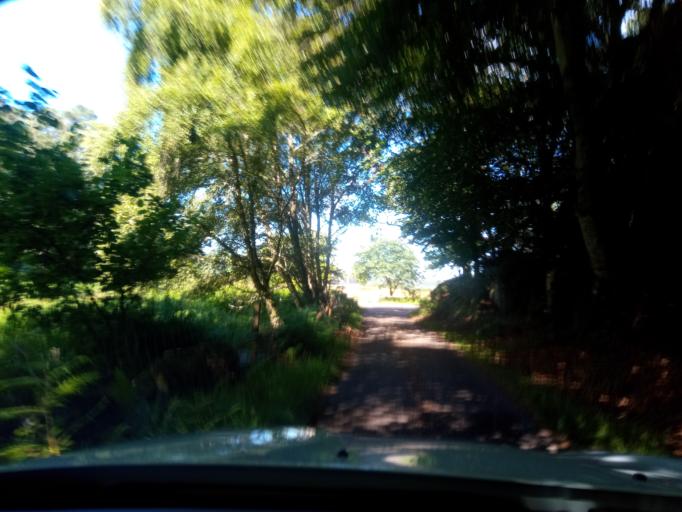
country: GB
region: Scotland
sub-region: Argyll and Bute
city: Isle Of Mull
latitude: 56.7580
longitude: -5.8104
